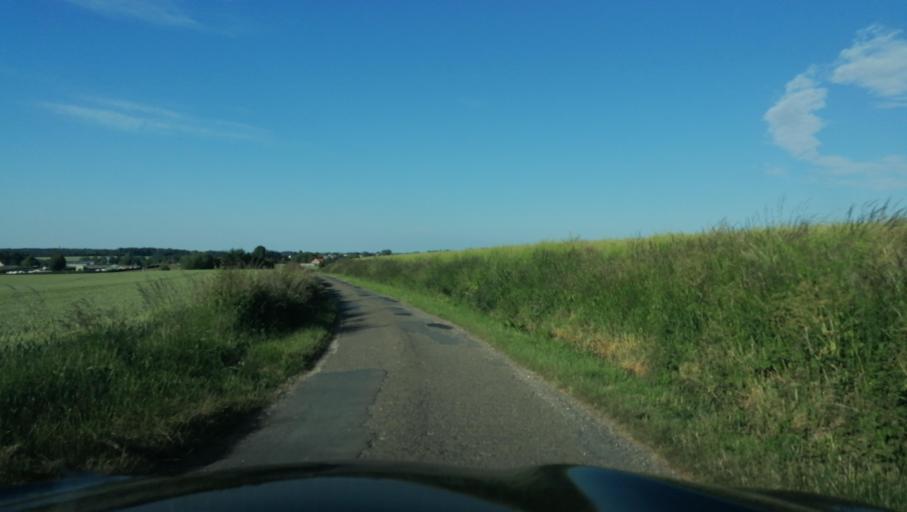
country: FR
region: Nord-Pas-de-Calais
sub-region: Departement du Nord
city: Recquignies
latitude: 50.2495
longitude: 4.0585
